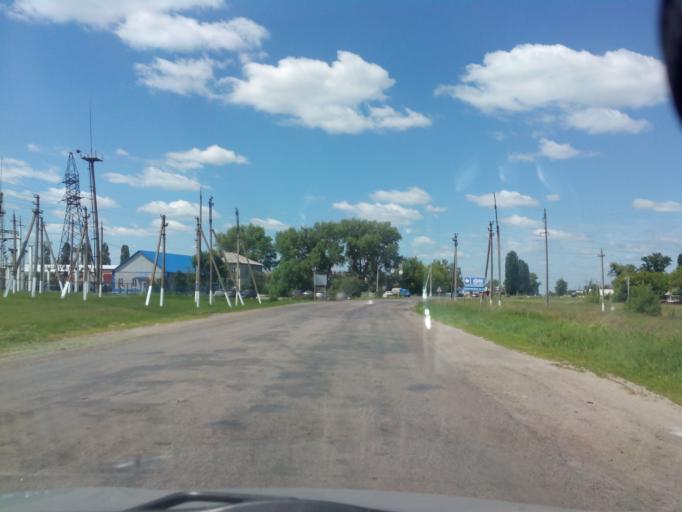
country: RU
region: Voronezj
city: Ternovka
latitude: 51.6770
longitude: 41.6031
